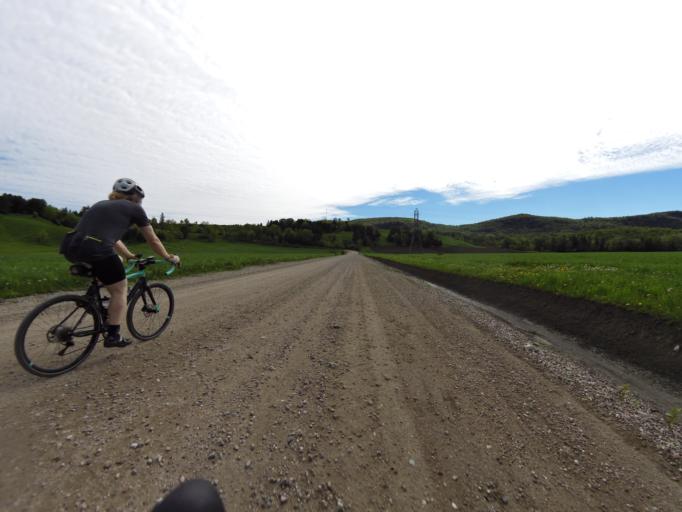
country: CA
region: Quebec
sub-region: Outaouais
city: Wakefield
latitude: 45.7294
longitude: -75.8952
